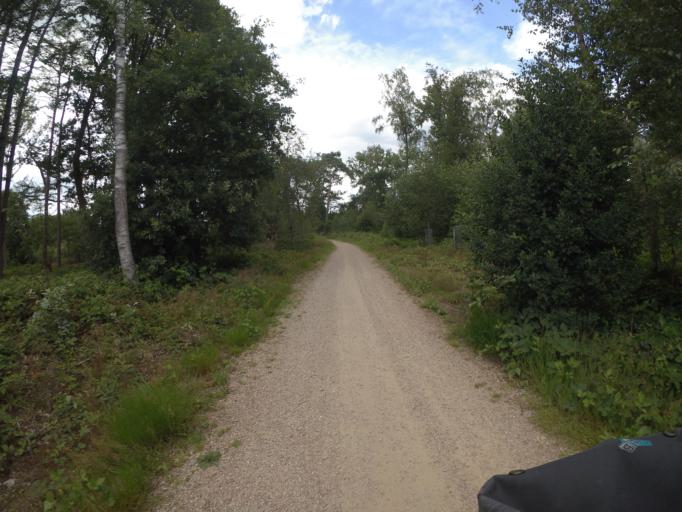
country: NL
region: North Brabant
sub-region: Gemeente Heeze-Leende
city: Heeze
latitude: 51.3955
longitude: 5.5902
